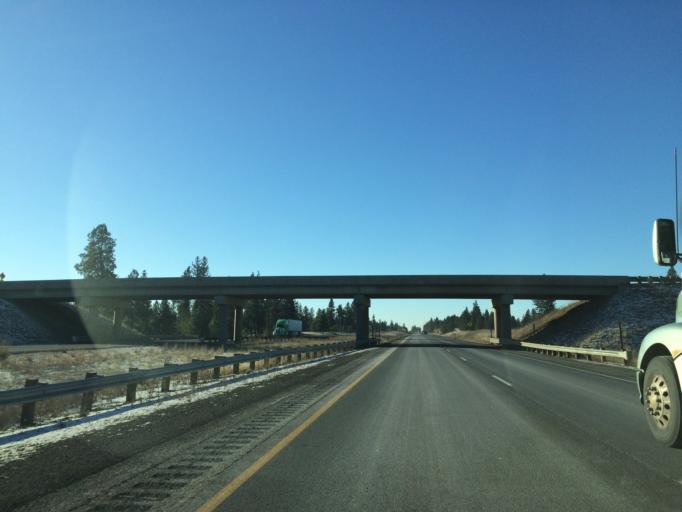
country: US
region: Washington
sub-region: Spokane County
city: Medical Lake
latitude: 47.4369
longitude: -117.7898
